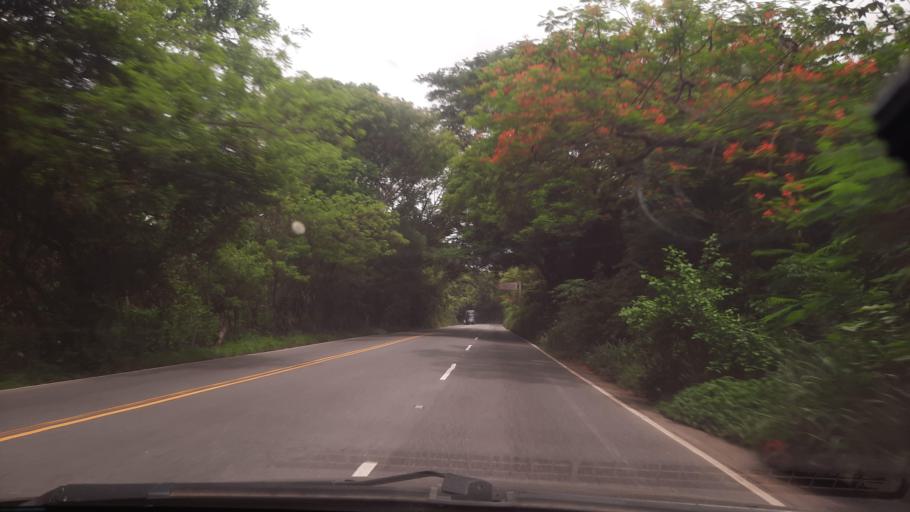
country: GT
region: Izabal
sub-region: Municipio de Los Amates
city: Los Amates
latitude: 15.2325
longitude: -89.2062
